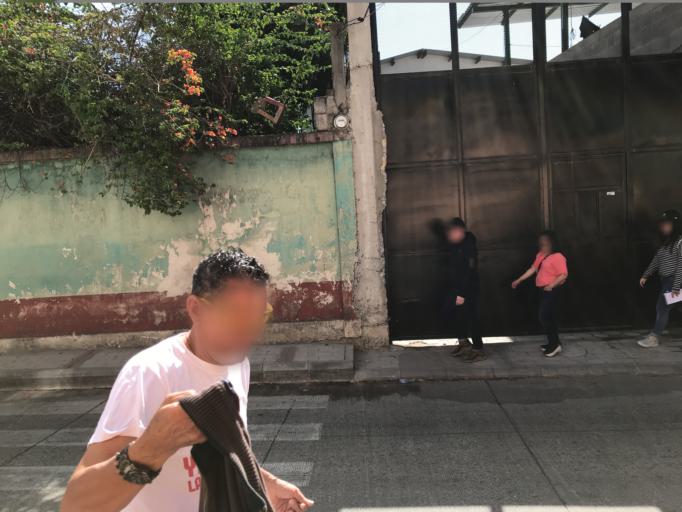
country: GT
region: Guatemala
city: Amatitlan
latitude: 14.4840
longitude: -90.6180
